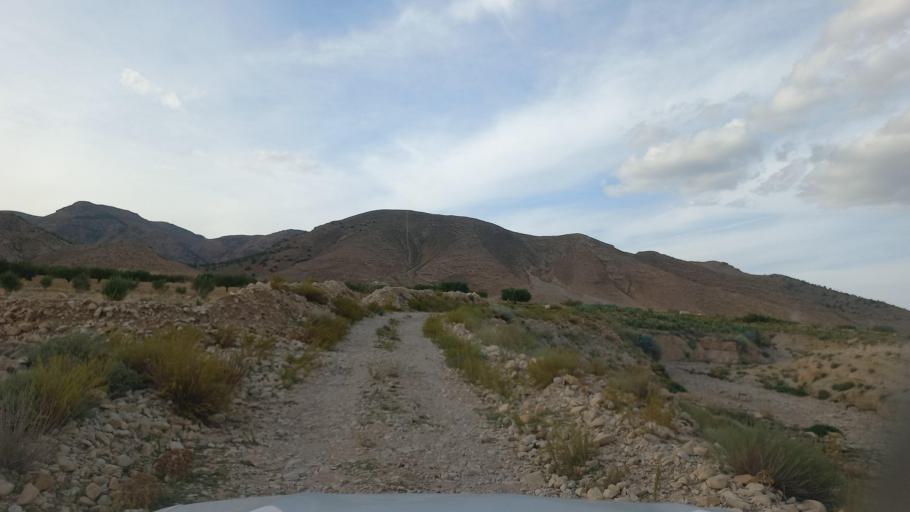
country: TN
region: Al Qasrayn
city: Sbiba
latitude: 35.4480
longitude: 9.0667
